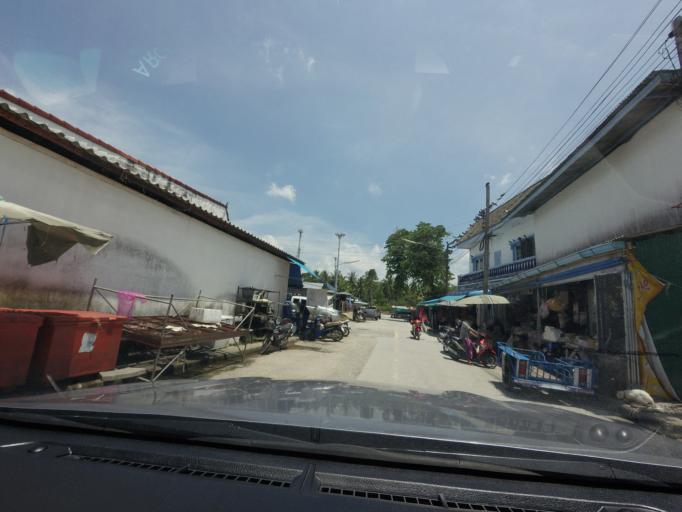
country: TH
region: Narathiwat
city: Rueso
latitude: 6.3953
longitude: 101.5155
